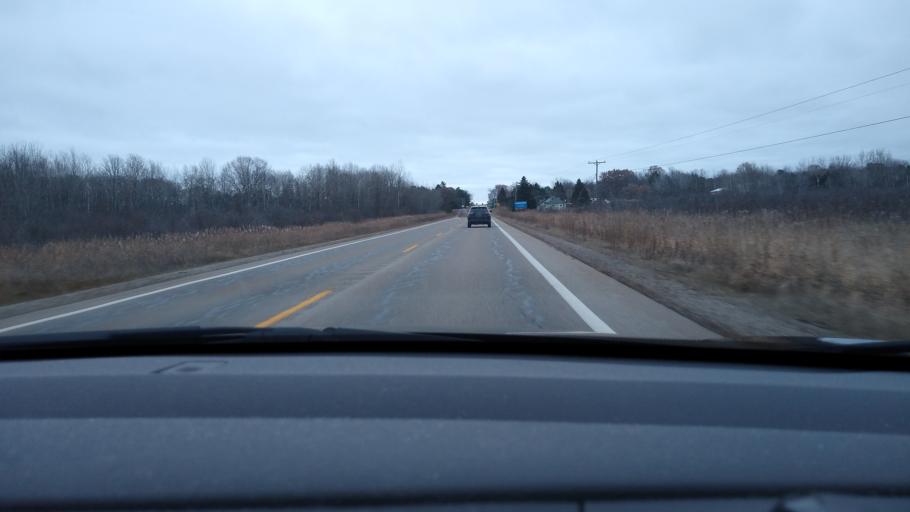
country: US
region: Michigan
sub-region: Roscommon County
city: Houghton Lake
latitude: 44.3358
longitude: -84.8208
